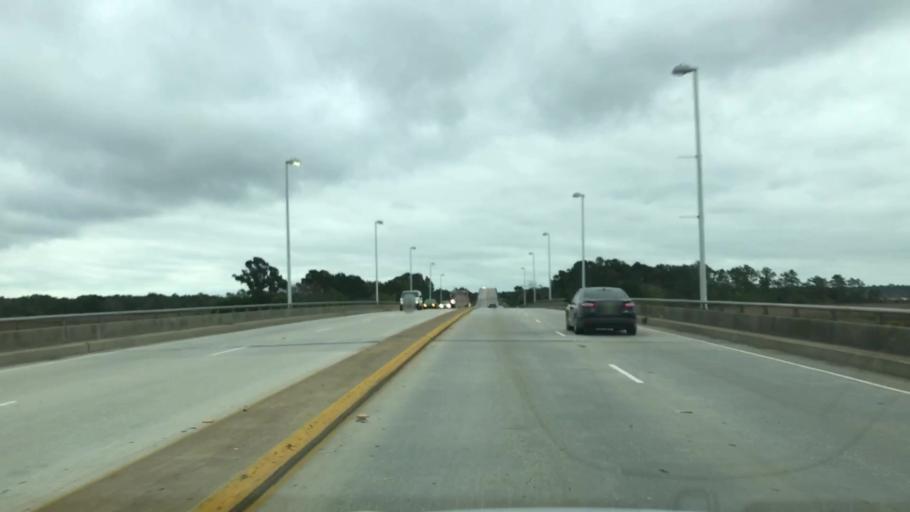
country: US
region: South Carolina
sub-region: Georgetown County
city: Georgetown
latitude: 33.3669
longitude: -79.2656
